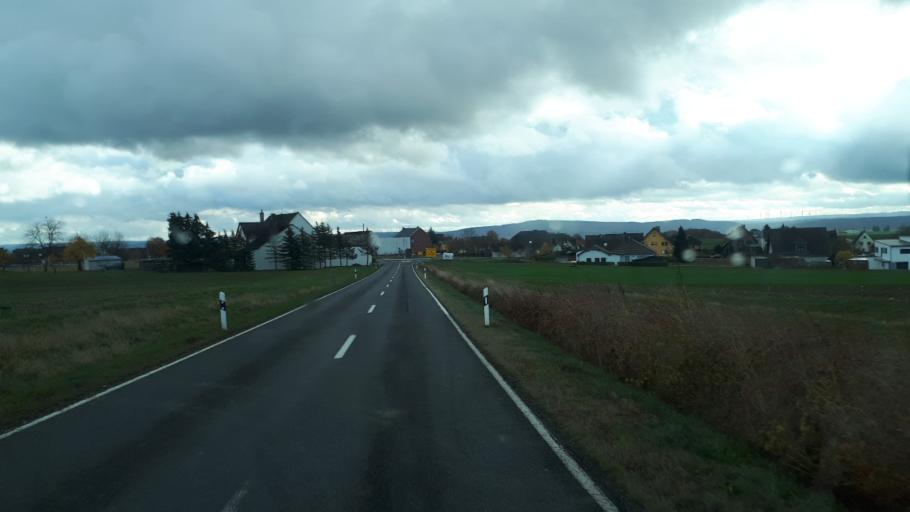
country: DE
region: Rheinland-Pfalz
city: Binningen
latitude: 50.2107
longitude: 7.2470
